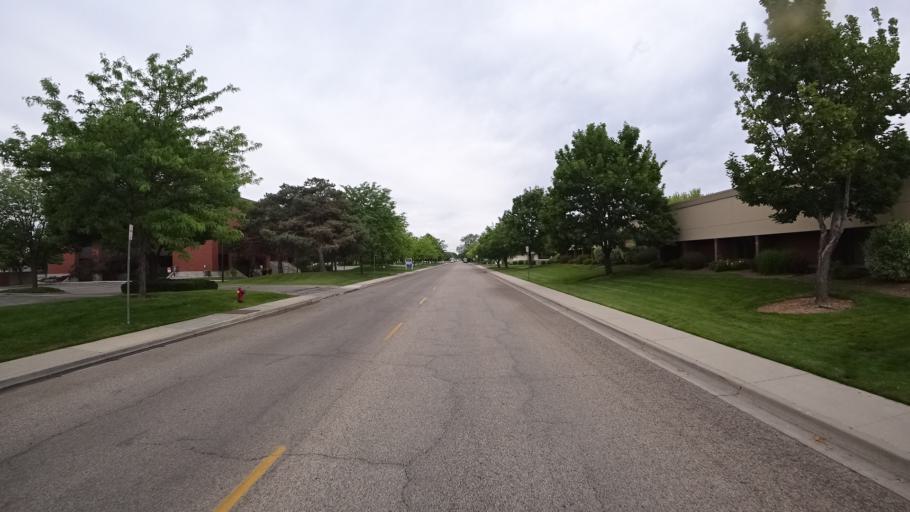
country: US
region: Idaho
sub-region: Ada County
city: Boise
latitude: 43.5735
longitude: -116.2214
